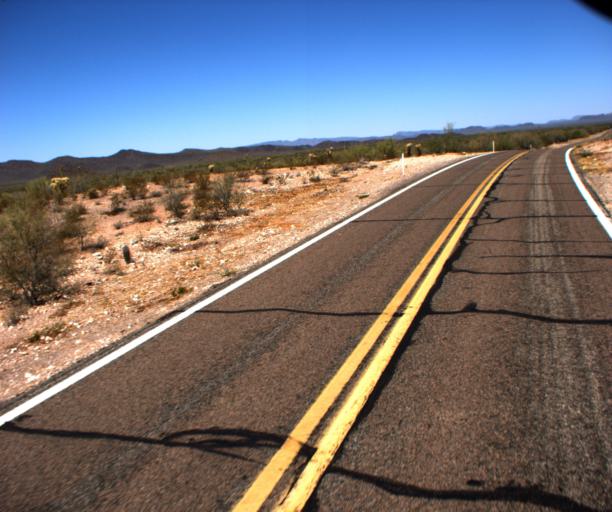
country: US
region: Arizona
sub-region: Pima County
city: Ajo
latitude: 32.2240
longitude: -112.7012
